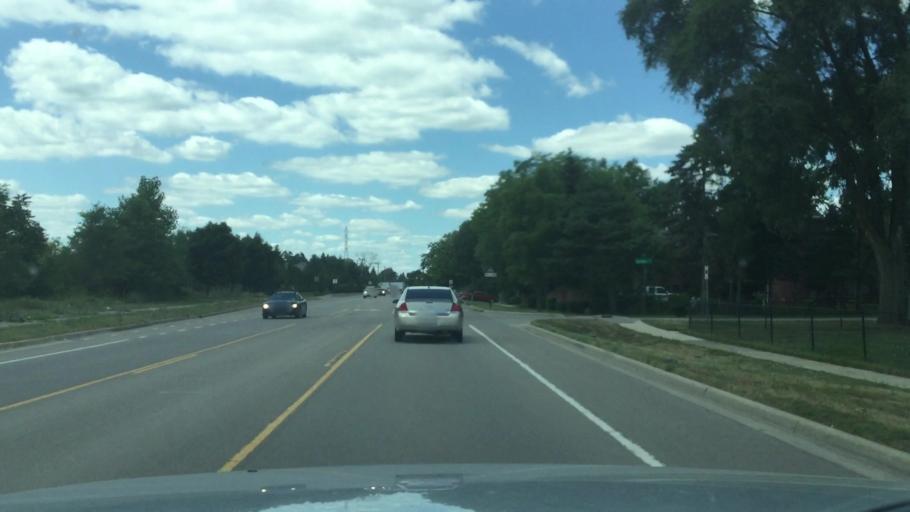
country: US
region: Michigan
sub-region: Washtenaw County
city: Ypsilanti
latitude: 42.2137
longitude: -83.5527
